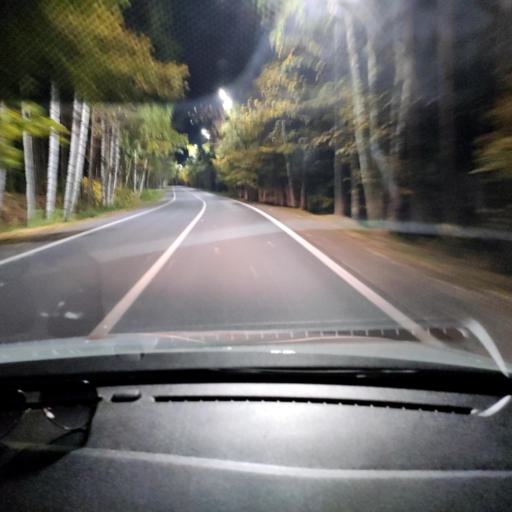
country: RU
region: Tatarstan
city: Verkhniy Uslon
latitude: 55.6306
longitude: 49.0162
